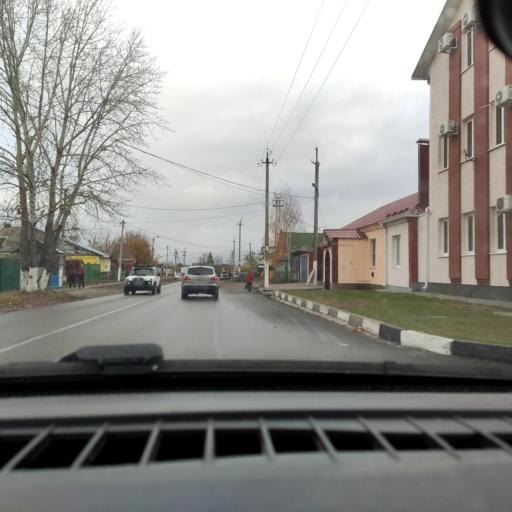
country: RU
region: Belgorod
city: Alekseyevka
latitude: 50.6304
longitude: 38.7014
